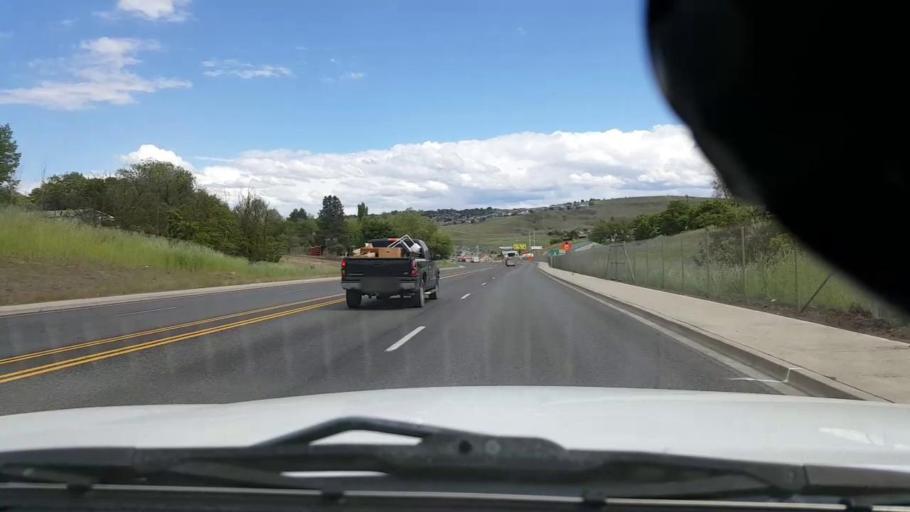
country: US
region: Washington
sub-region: Asotin County
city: West Clarkston-Highland
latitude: 46.4001
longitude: -117.0522
